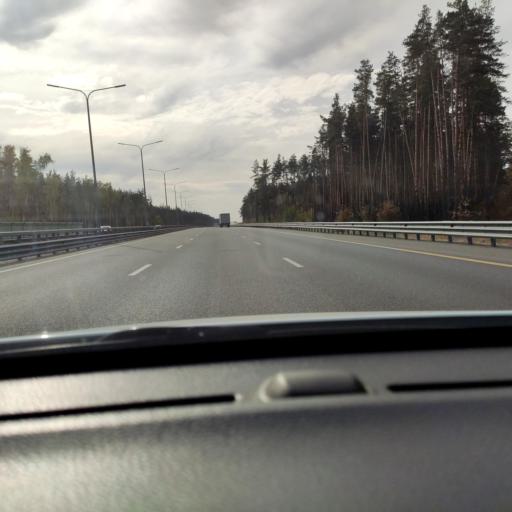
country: RU
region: Voronezj
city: Somovo
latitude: 51.7115
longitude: 39.3072
